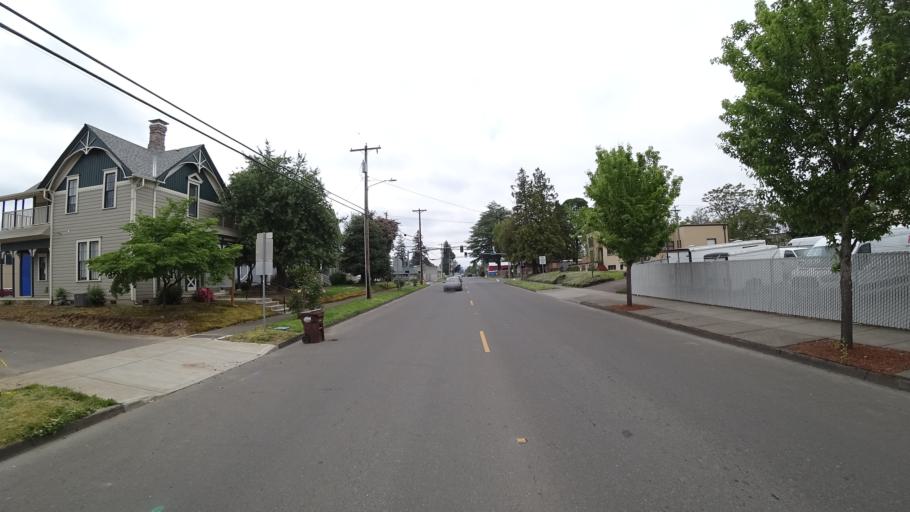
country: US
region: Oregon
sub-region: Washington County
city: Hillsboro
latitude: 45.5176
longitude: -122.9890
